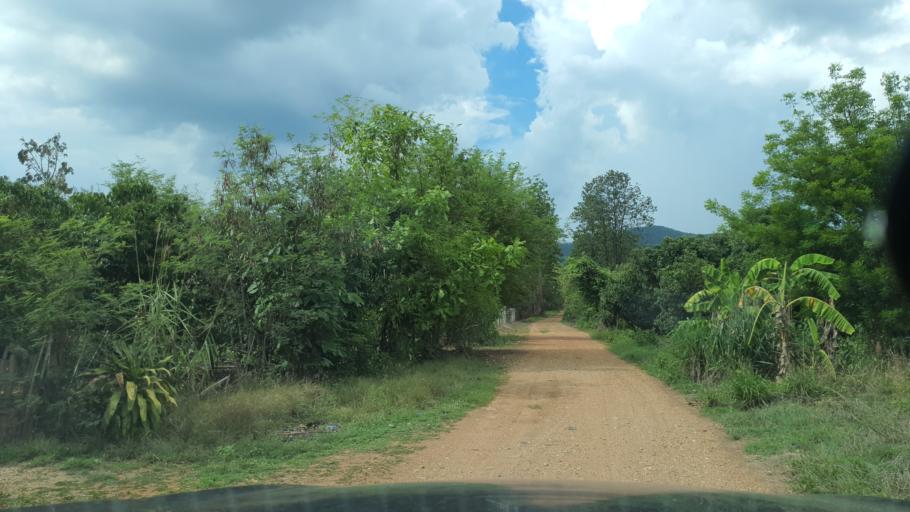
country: TH
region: Chiang Mai
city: Mae Taeng
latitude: 19.1327
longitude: 99.0335
